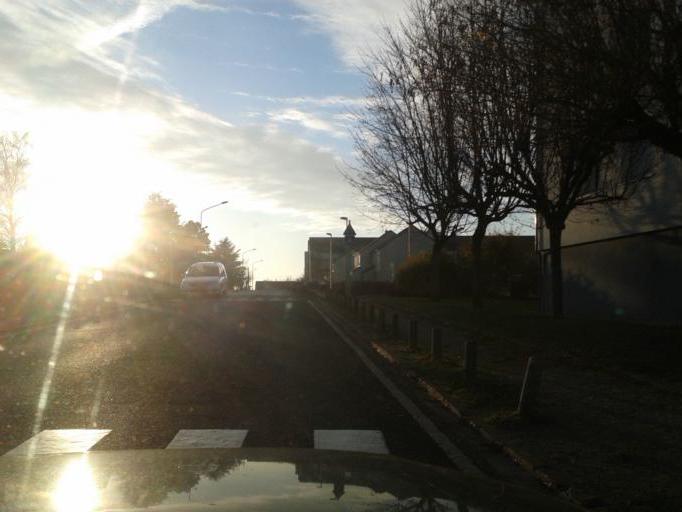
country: FR
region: Centre
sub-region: Departement du Loiret
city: Beaugency
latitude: 47.7719
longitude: 1.6244
